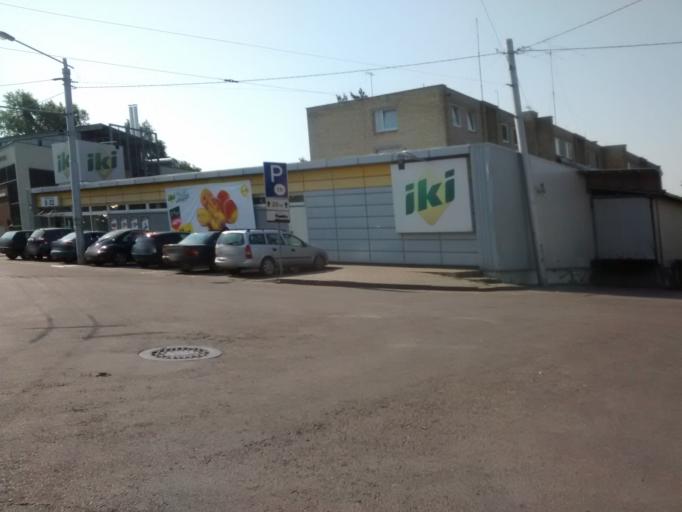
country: LT
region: Kauno apskritis
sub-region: Kaunas
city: Eiguliai
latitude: 54.9144
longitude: 23.9206
